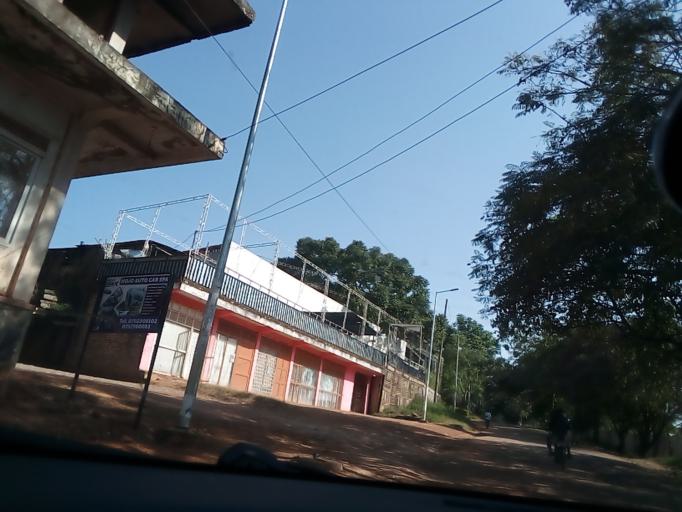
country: UG
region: Central Region
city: Masaka
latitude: -0.3406
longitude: 31.7364
